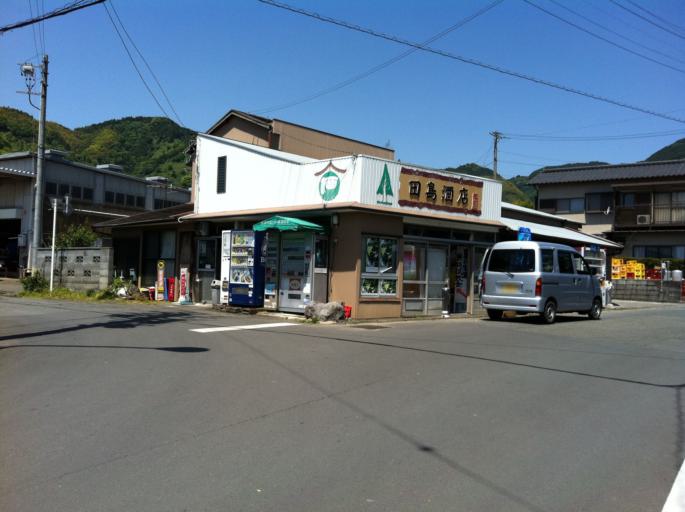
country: JP
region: Shizuoka
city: Shizuoka-shi
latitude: 35.0433
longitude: 138.4506
